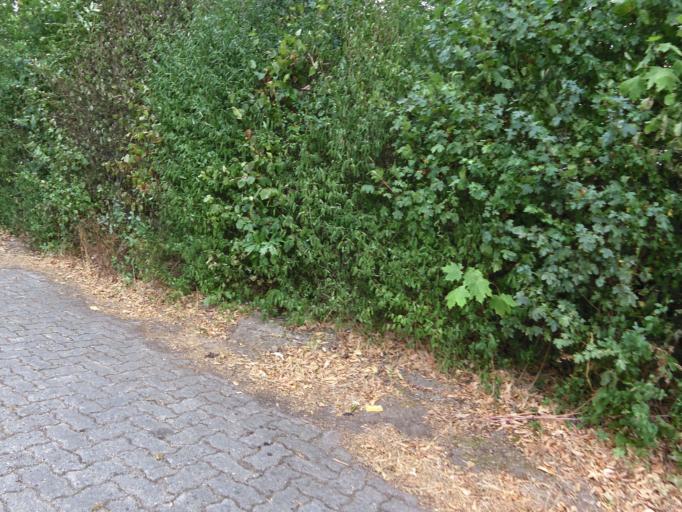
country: DE
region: Bavaria
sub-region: Regierungsbezirk Unterfranken
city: Veitshochheim
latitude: 49.8265
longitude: 9.8889
